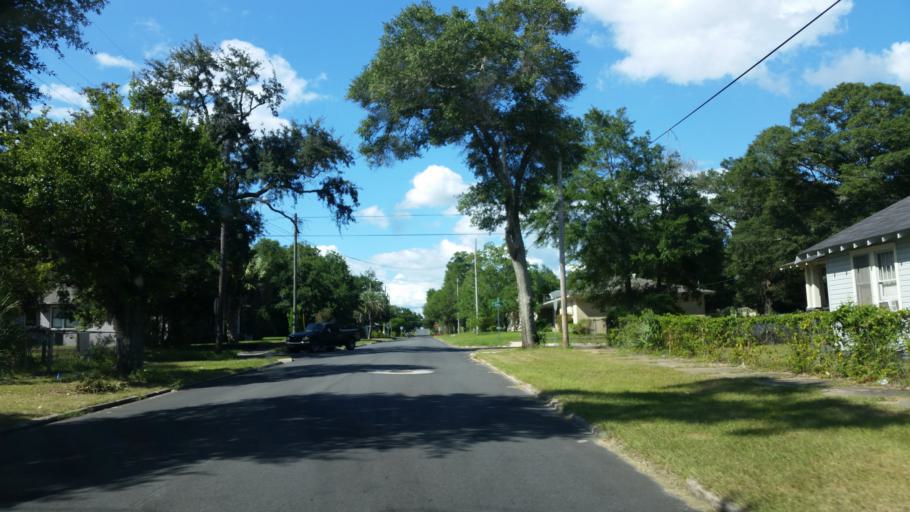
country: US
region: Florida
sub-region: Escambia County
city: Pensacola
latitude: 30.4123
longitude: -87.2306
